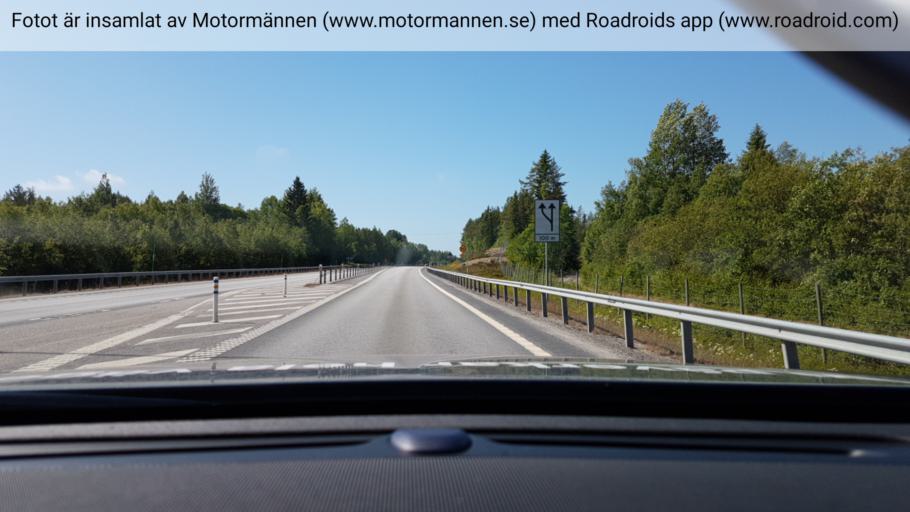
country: SE
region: Vaesterbotten
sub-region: Umea Kommun
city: Roback
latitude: 63.7541
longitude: 20.1556
